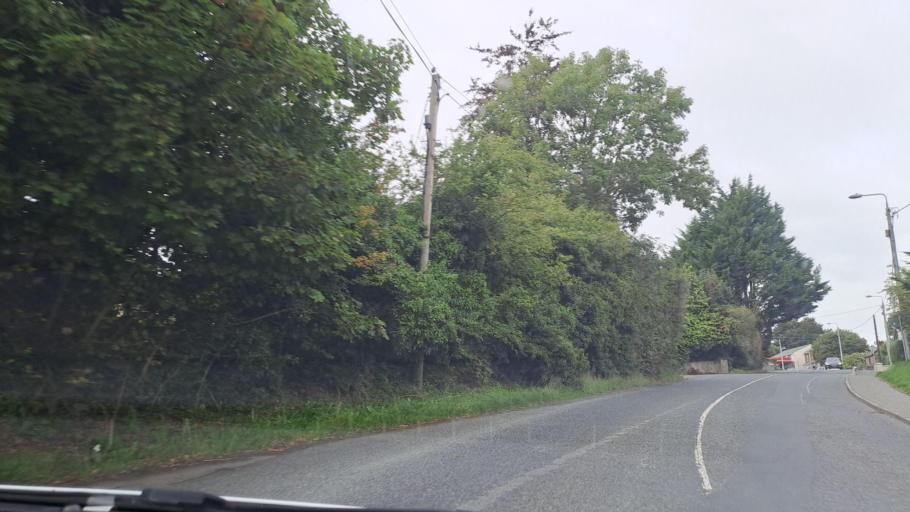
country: IE
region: Ulster
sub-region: An Cabhan
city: Kingscourt
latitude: 53.9053
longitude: -6.8000
